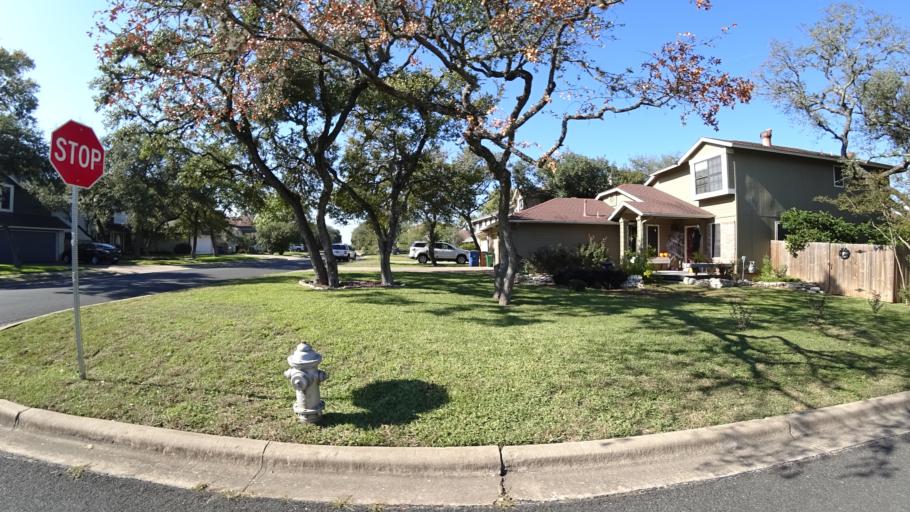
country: US
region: Texas
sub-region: Travis County
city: Shady Hollow
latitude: 30.1995
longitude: -97.8485
